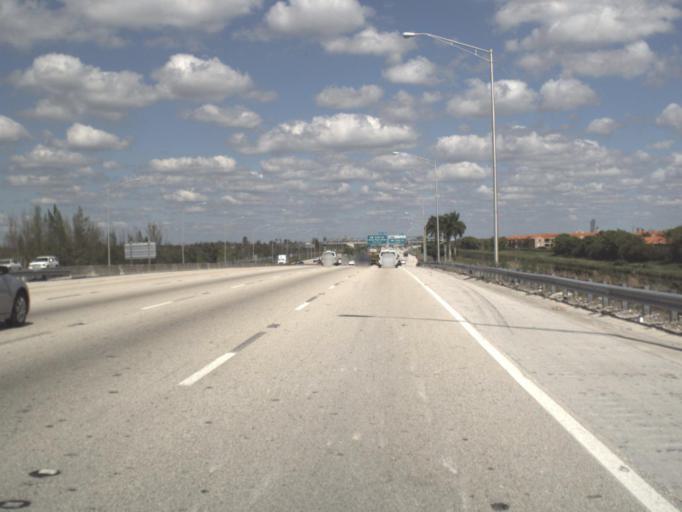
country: US
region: Florida
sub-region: Miami-Dade County
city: Doral
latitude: 25.8265
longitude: -80.3866
